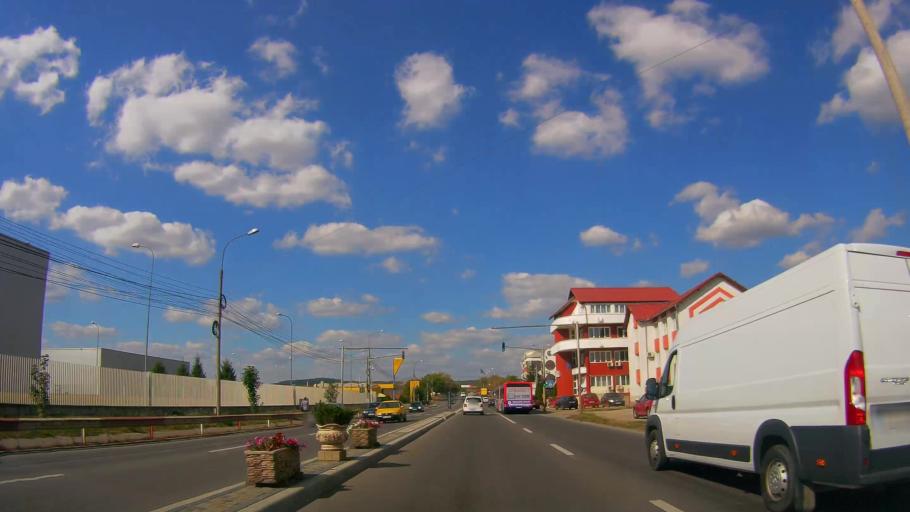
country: RO
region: Salaj
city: Zalau
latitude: 47.2137
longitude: 23.0429
